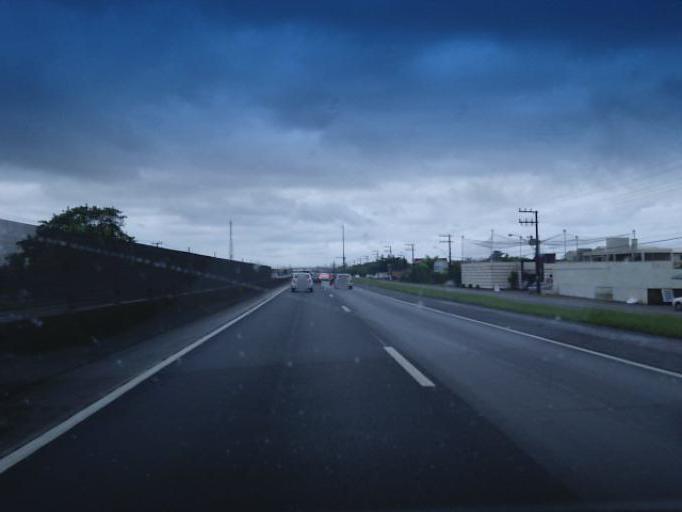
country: BR
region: Santa Catarina
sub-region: Barra Velha
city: Barra Velha
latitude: -26.6719
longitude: -48.6901
